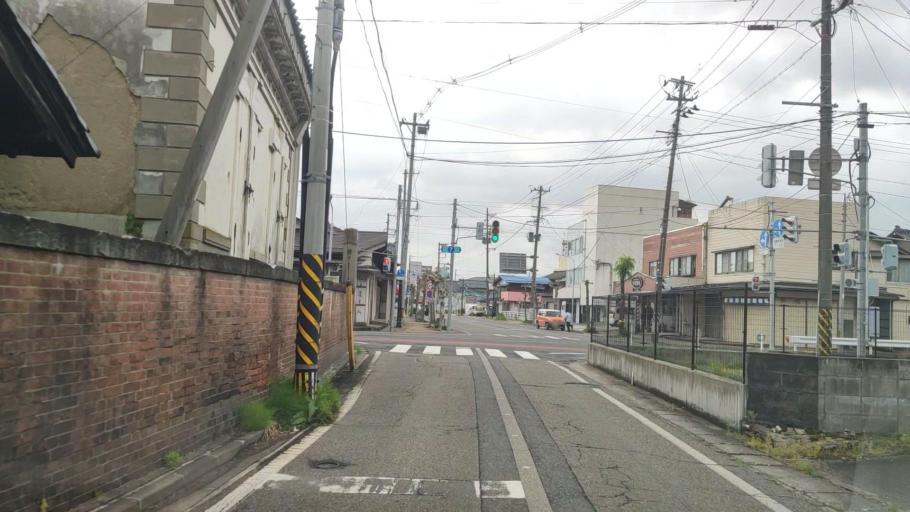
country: JP
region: Niigata
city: Gosen
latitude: 37.7376
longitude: 139.1761
